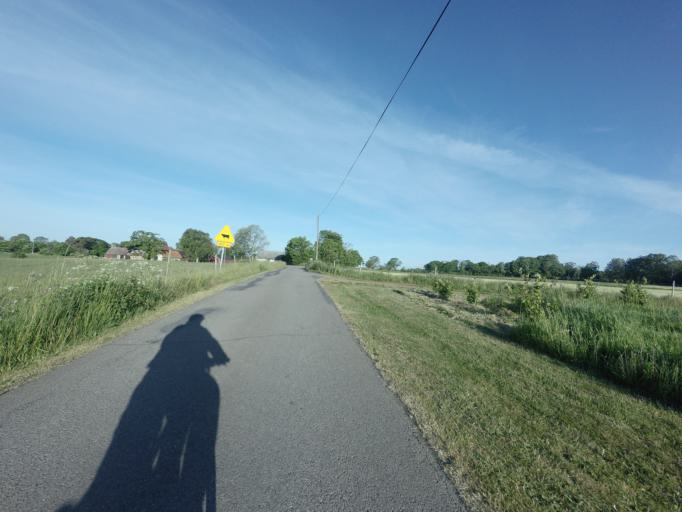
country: SE
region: Skane
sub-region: Hoganas Kommun
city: Hoganas
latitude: 56.2453
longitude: 12.6532
